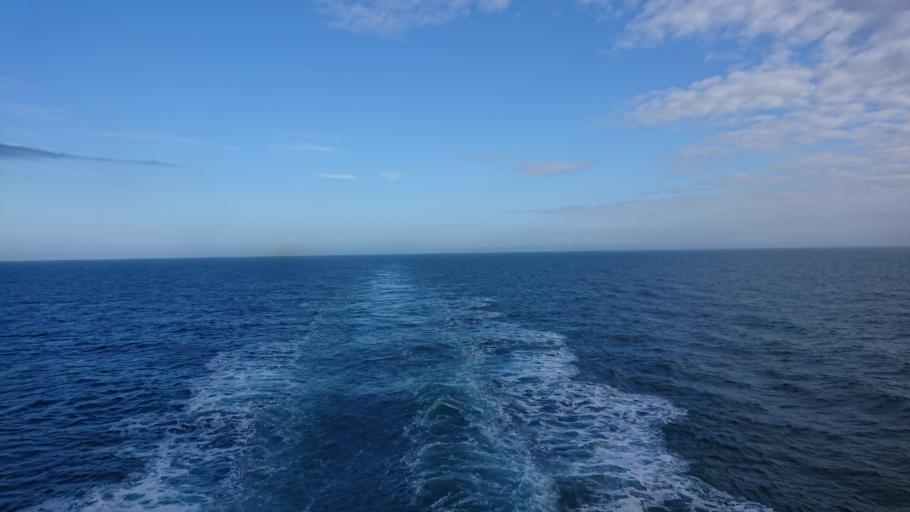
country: GB
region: Wales
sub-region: Pembrokeshire
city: Saint David's
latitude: 52.1313
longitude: -5.5985
